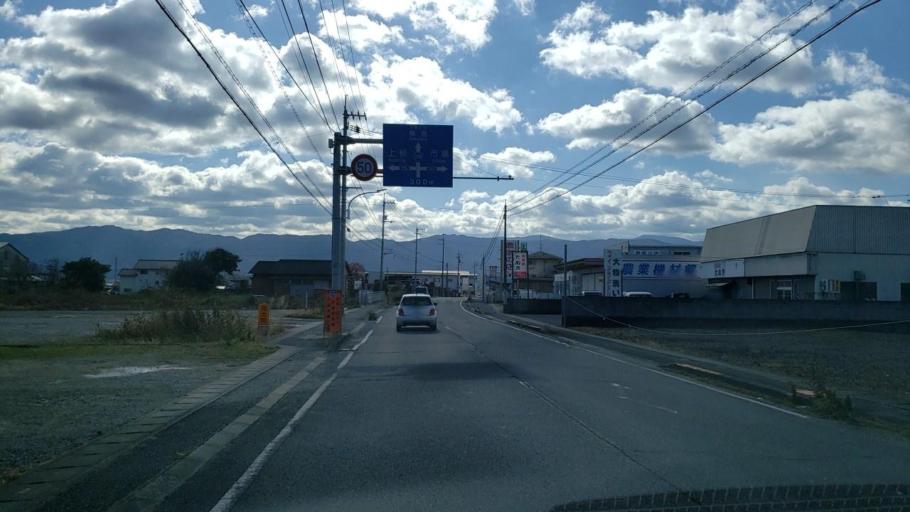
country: JP
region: Tokushima
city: Kamojimacho-jogejima
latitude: 34.0995
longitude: 134.3450
